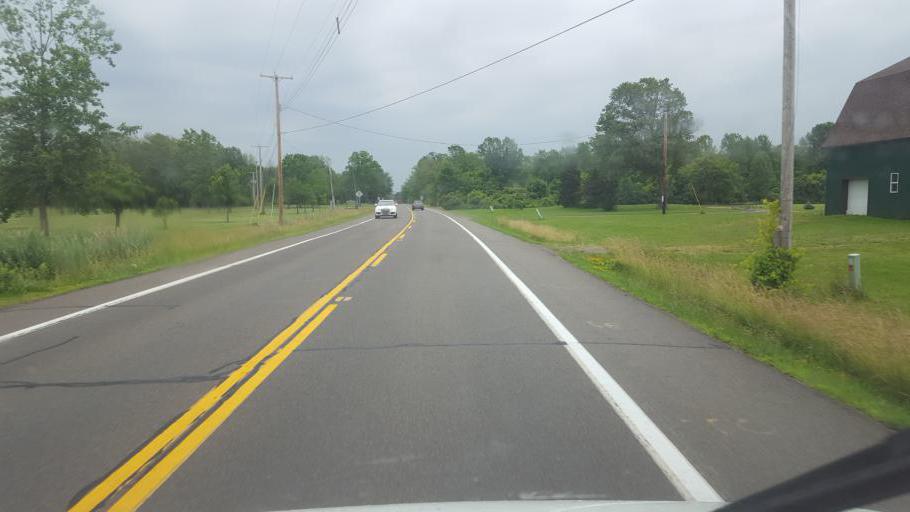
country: US
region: New York
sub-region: Niagara County
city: Wilson
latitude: 43.3071
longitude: -78.8550
